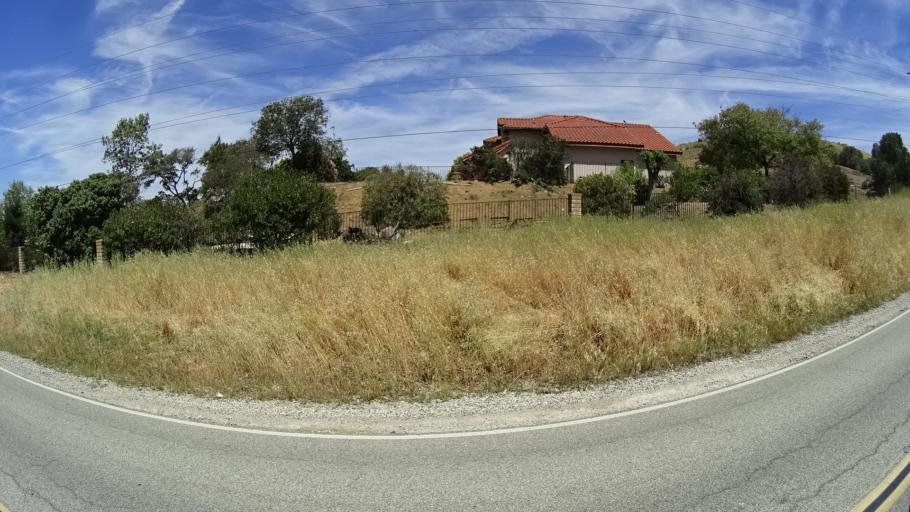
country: US
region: California
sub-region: Ventura County
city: Casa Conejo
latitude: 34.1542
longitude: -118.9470
